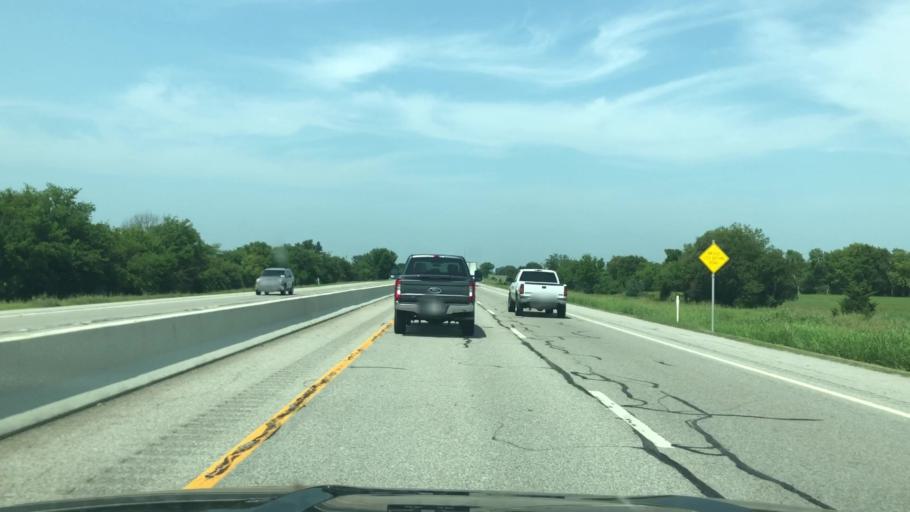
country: US
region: Oklahoma
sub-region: Ottawa County
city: Fairland
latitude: 36.7823
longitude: -94.8890
